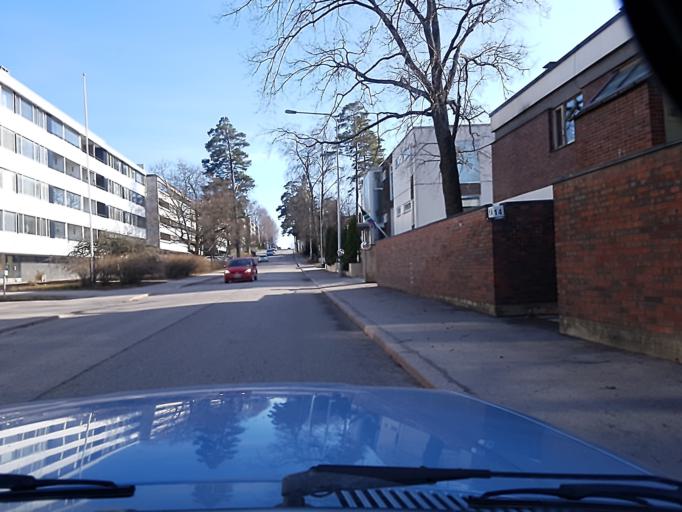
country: FI
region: Uusimaa
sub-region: Helsinki
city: Teekkarikylae
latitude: 60.1673
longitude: 24.8576
